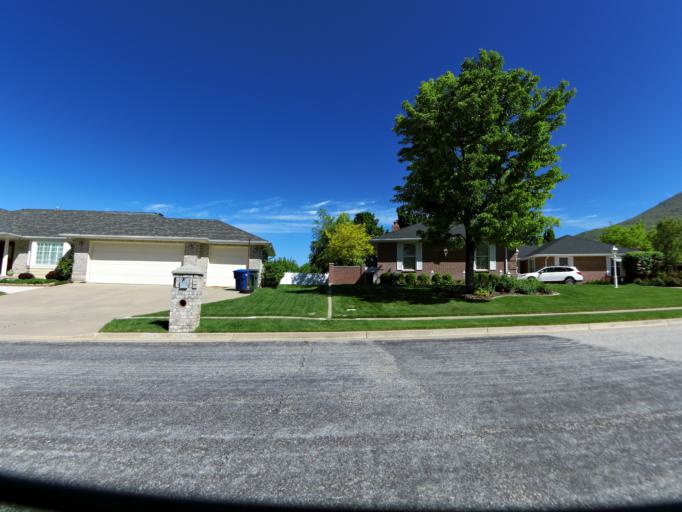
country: US
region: Utah
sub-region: Weber County
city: Uintah
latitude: 41.1655
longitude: -111.9330
